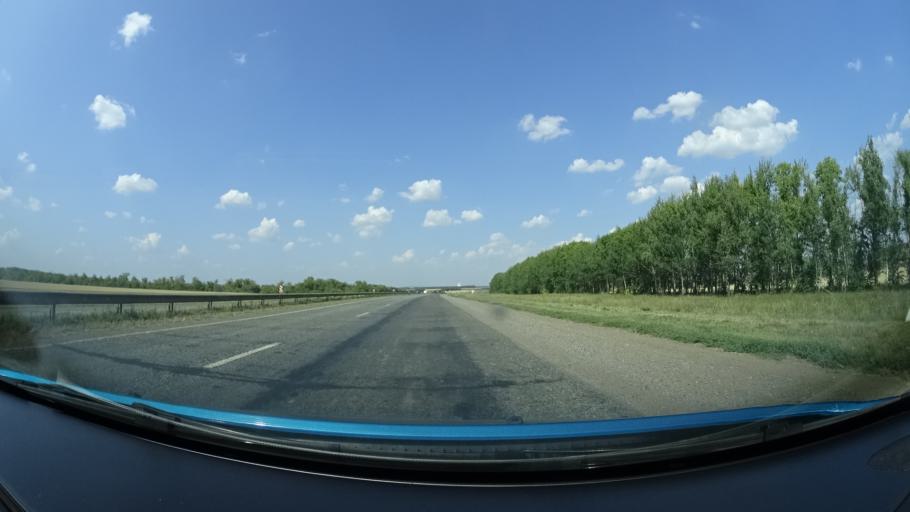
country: RU
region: Bashkortostan
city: Dmitriyevka
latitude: 54.6751
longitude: 55.3578
